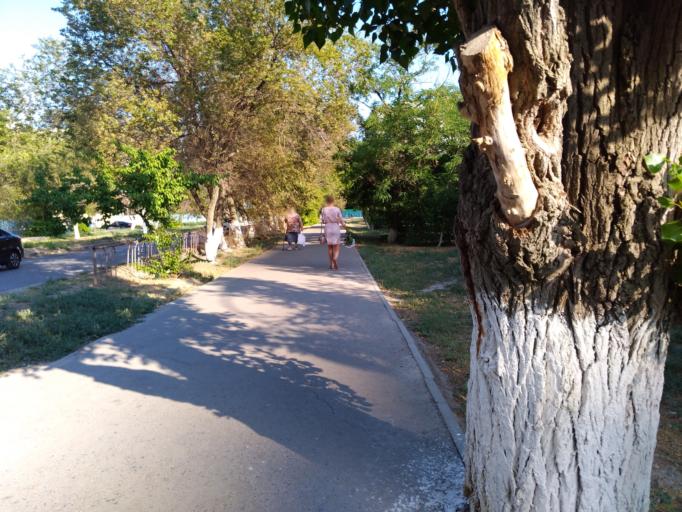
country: RU
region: Volgograd
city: Volgograd
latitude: 48.7209
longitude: 44.5130
